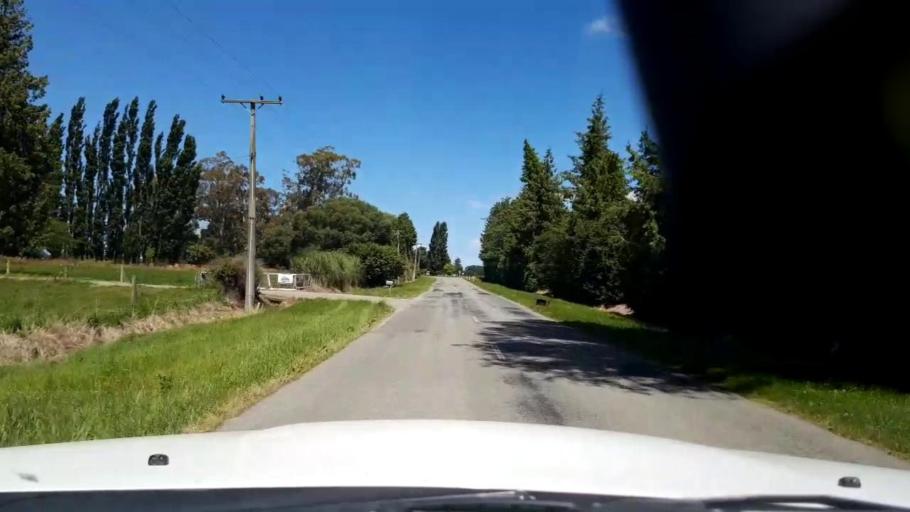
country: NZ
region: Canterbury
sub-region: Timaru District
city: Pleasant Point
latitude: -44.1599
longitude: 171.3052
